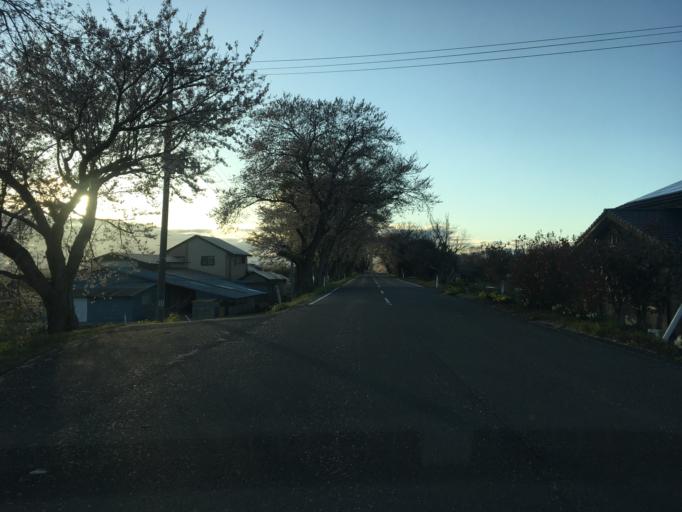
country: JP
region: Miyagi
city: Wakuya
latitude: 38.6442
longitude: 141.1648
